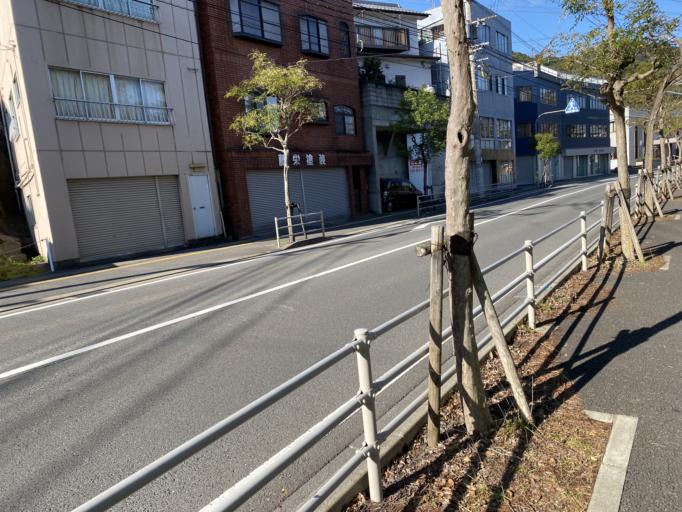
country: JP
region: Nagasaki
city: Nagasaki-shi
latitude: 32.7571
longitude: 129.8617
